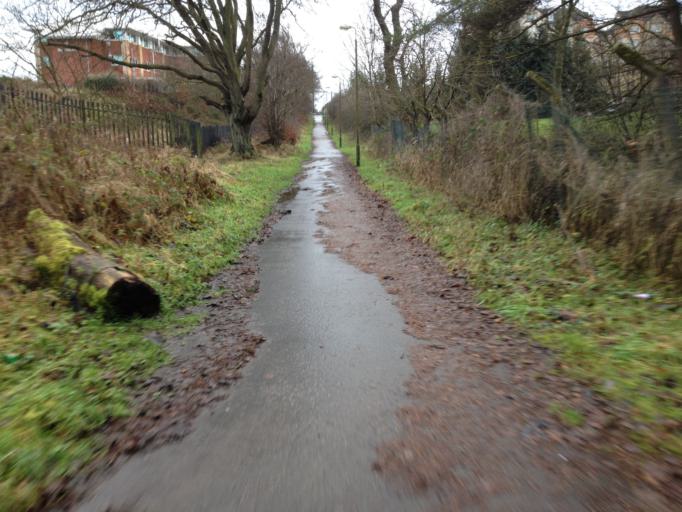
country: GB
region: Scotland
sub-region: West Lothian
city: Livingston
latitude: 55.9163
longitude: -3.5306
